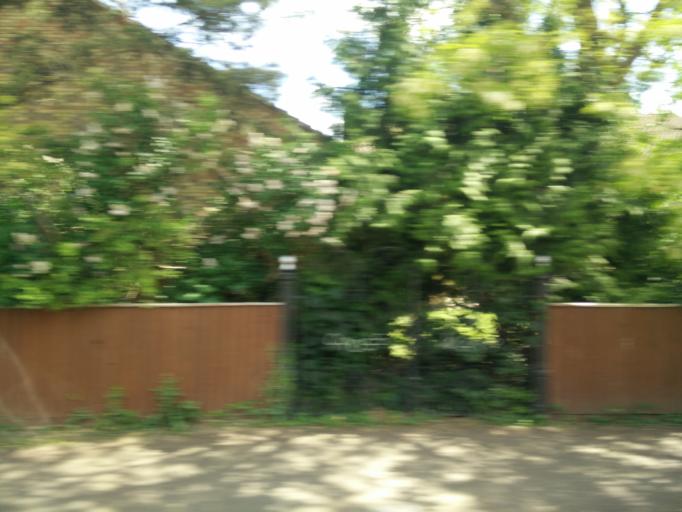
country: GB
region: England
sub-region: Cambridgeshire
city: Grantchester
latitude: 52.1726
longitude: 0.1128
